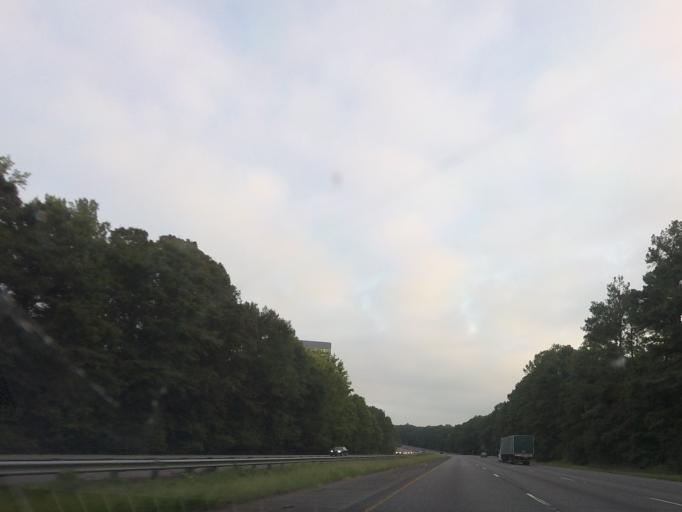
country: US
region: Georgia
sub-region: Monroe County
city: Forsyth
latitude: 33.1187
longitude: -84.0039
